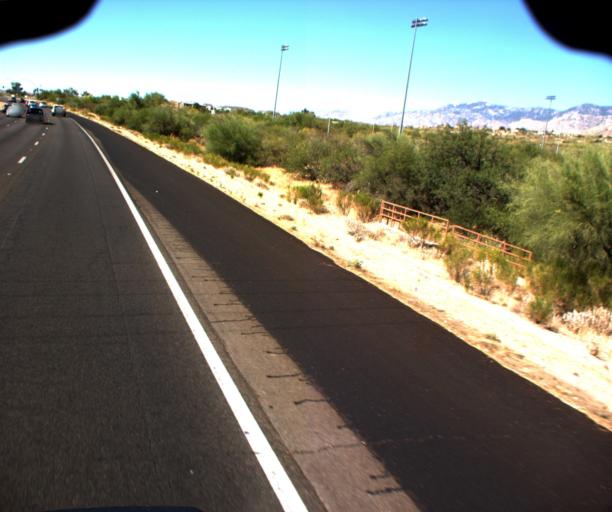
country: US
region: Arizona
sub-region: Pima County
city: Oro Valley
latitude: 32.3775
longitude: -110.9647
